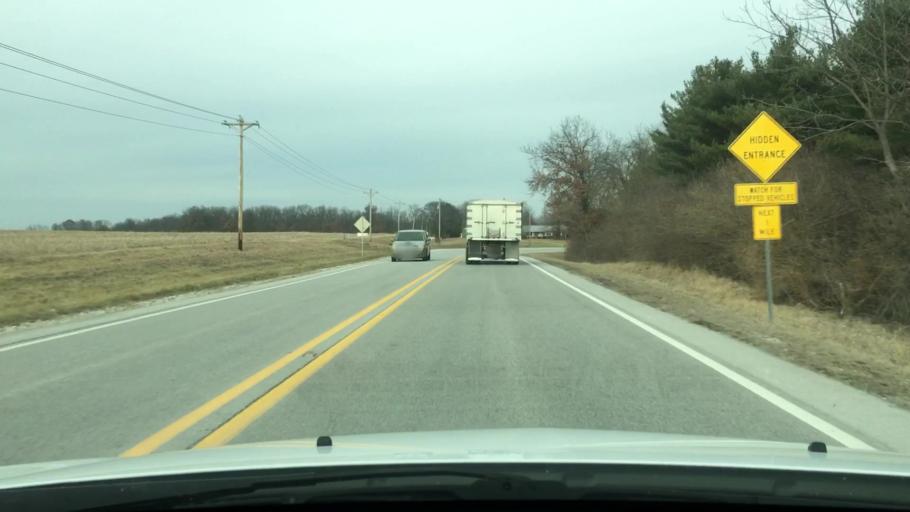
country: US
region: Illinois
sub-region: Pike County
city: Pittsfield
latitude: 39.6513
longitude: -90.7841
